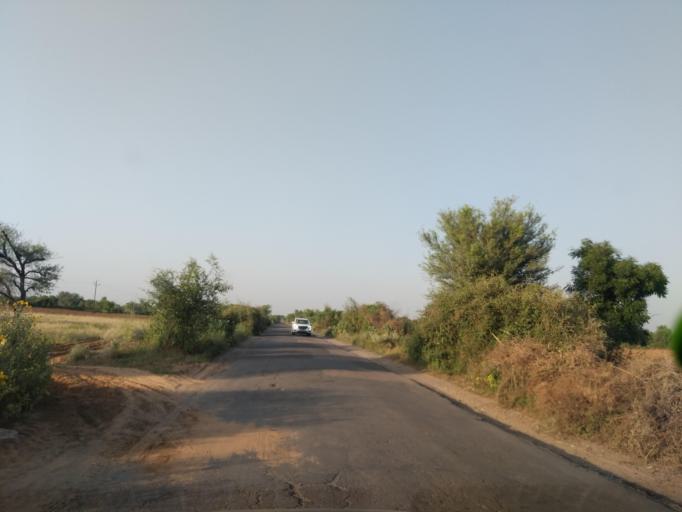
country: IN
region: Rajasthan
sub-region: Churu
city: Rajgarh
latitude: 28.5730
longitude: 75.3695
